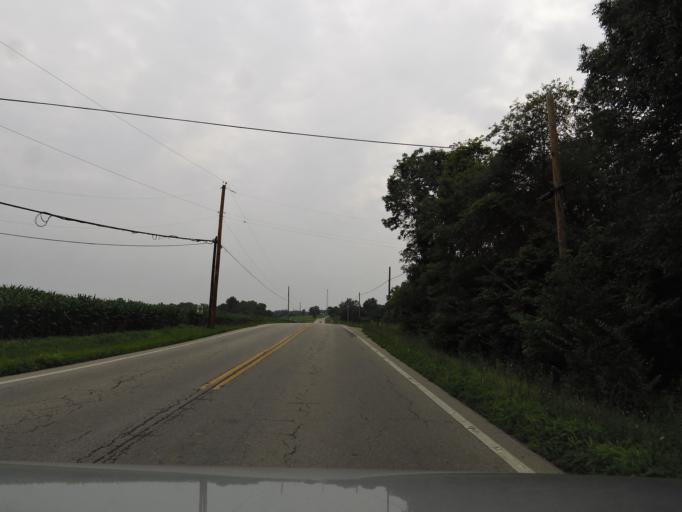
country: US
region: Ohio
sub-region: Clinton County
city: Wilmington
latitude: 39.3527
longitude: -83.8768
